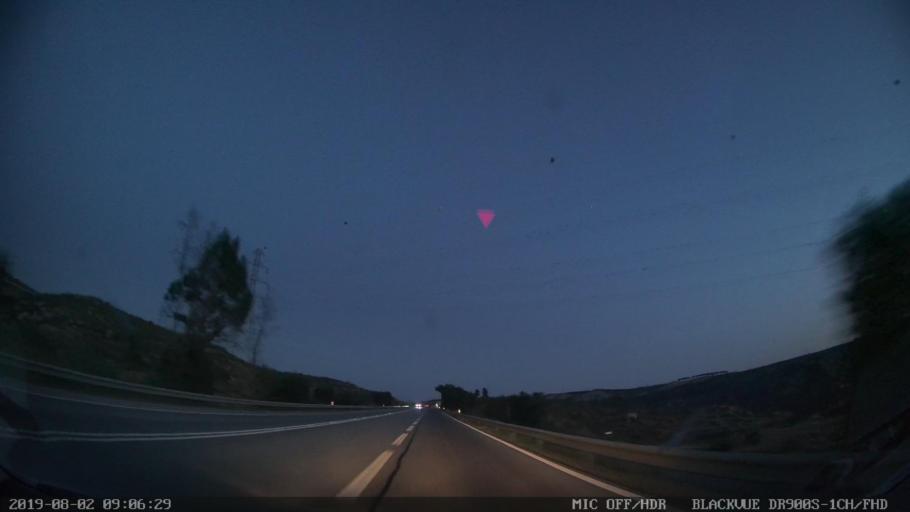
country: PT
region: Portalegre
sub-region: Nisa
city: Nisa
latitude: 39.5262
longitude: -7.7851
